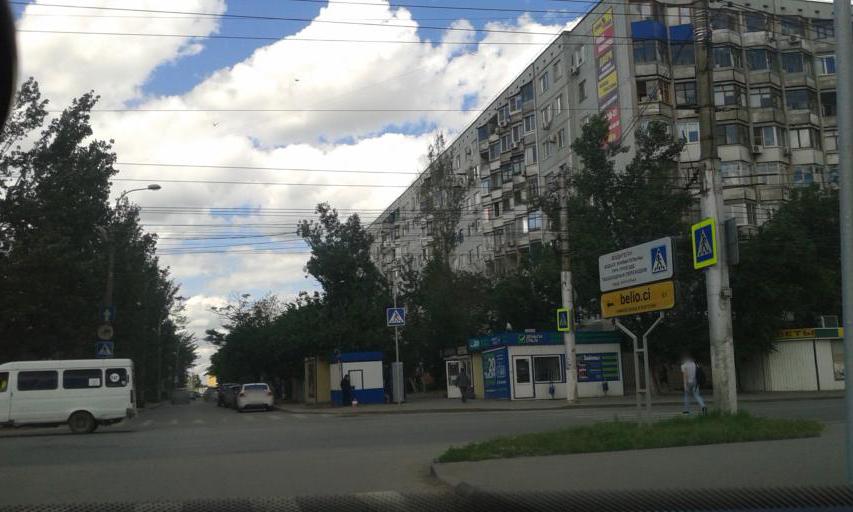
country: RU
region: Volgograd
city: Volgograd
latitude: 48.7541
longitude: 44.5038
